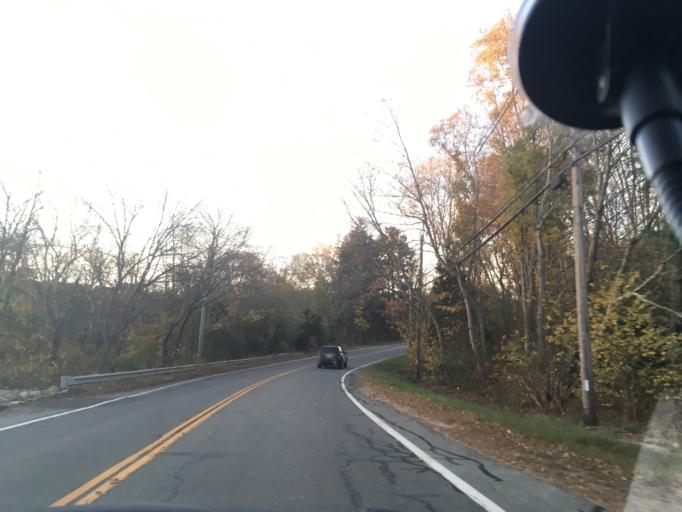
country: US
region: Rhode Island
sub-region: Washington County
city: North Kingstown
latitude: 41.5629
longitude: -71.4642
